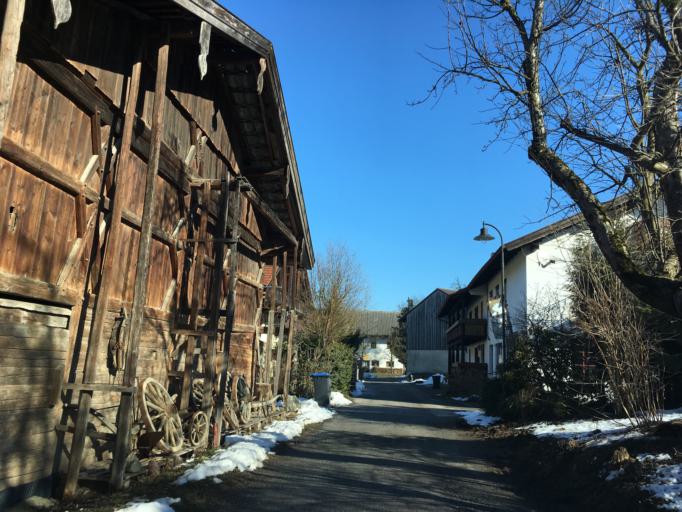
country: DE
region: Bavaria
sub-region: Upper Bavaria
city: Vogtareuth
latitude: 47.9477
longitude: 12.1795
